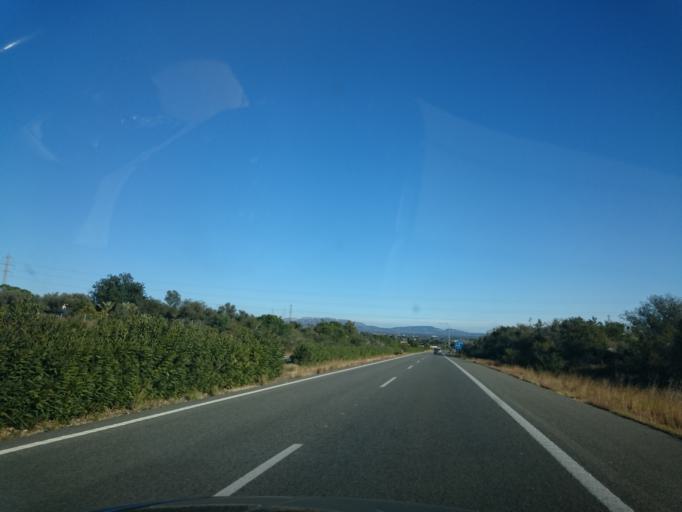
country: ES
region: Catalonia
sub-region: Provincia de Tarragona
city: Masdenverge
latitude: 40.7099
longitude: 0.5536
